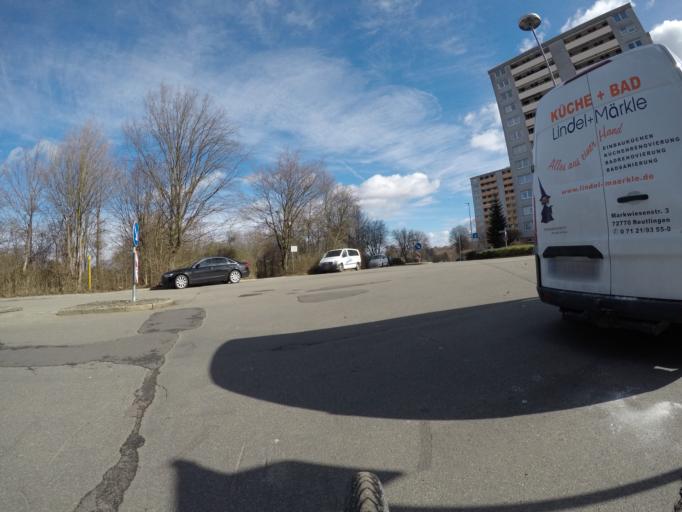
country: DE
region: Baden-Wuerttemberg
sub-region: Tuebingen Region
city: Sickenhausen
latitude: 48.5239
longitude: 9.2036
